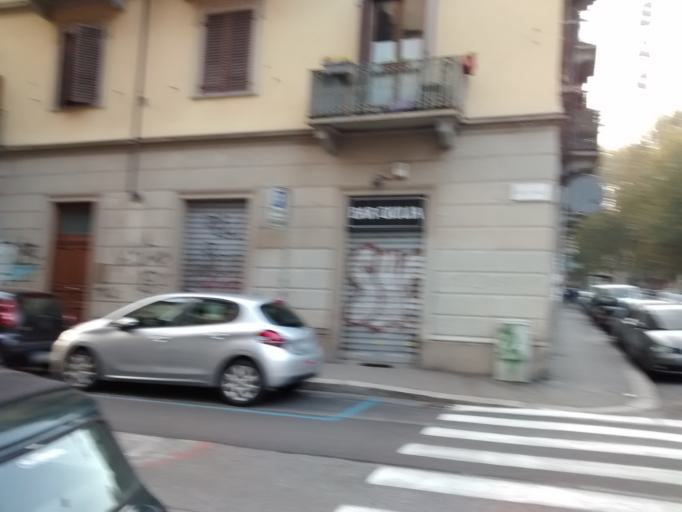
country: IT
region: Piedmont
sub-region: Provincia di Torino
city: Turin
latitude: 45.0714
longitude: 7.6979
